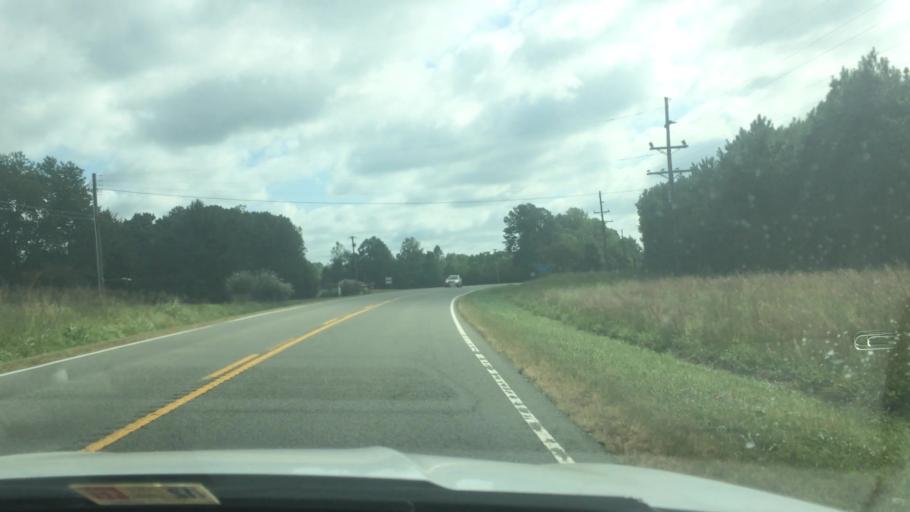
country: US
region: Virginia
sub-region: Lancaster County
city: Lancaster
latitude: 37.8390
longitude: -76.5777
